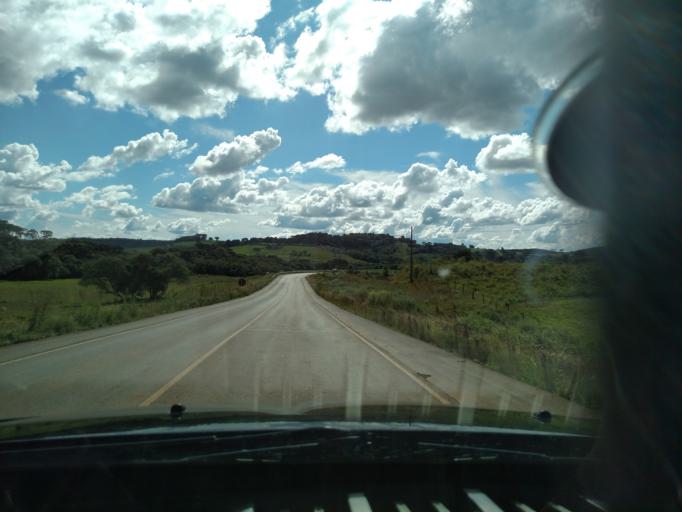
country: BR
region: Rio Grande do Sul
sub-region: Vacaria
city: Estrela
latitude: -27.9083
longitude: -50.7212
